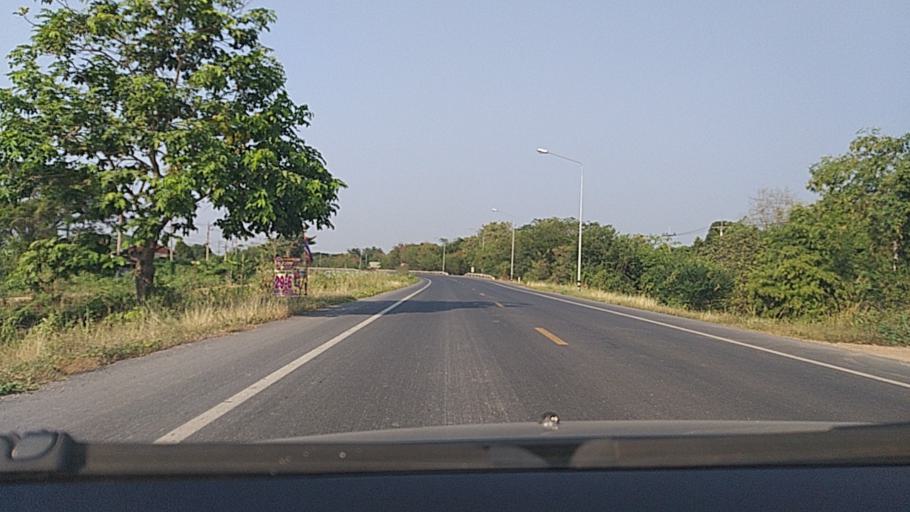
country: TH
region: Sing Buri
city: Phrom Buri
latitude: 14.8101
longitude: 100.4349
